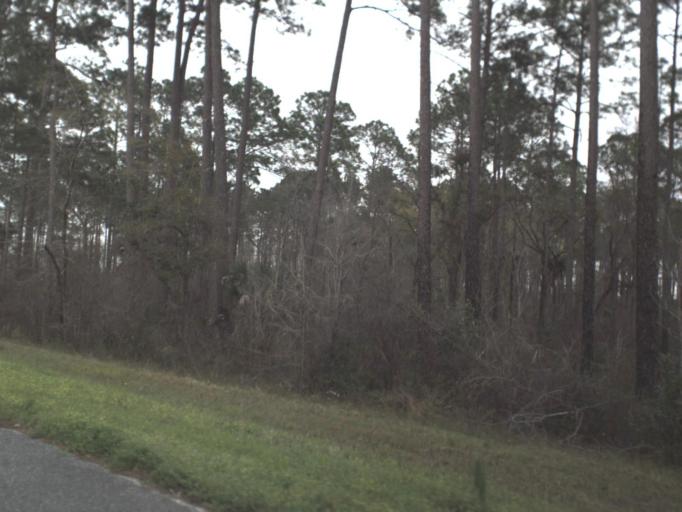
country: US
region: Florida
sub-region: Franklin County
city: Eastpoint
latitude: 29.8227
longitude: -84.9062
